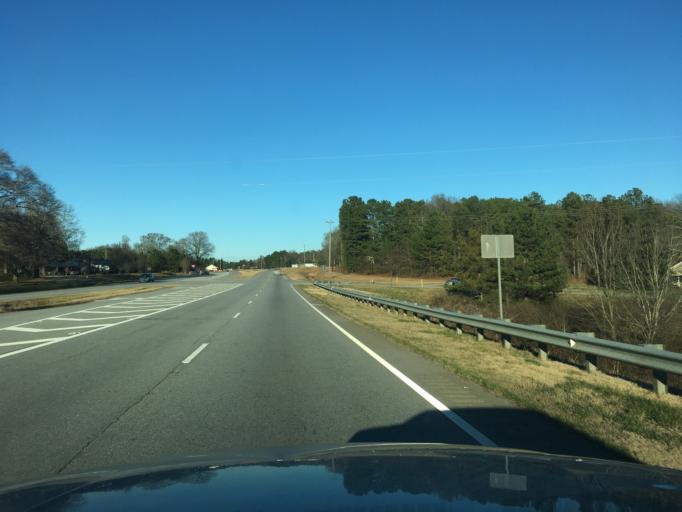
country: US
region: Georgia
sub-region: Carroll County
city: Carrollton
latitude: 33.4961
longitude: -85.0855
